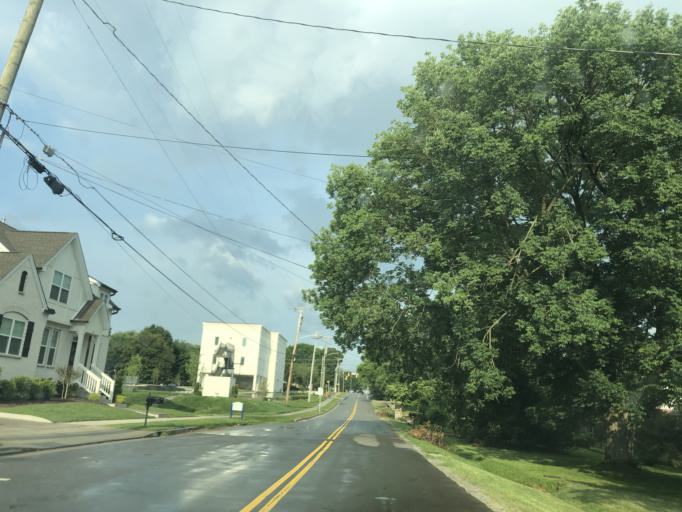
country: US
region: Tennessee
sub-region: Davidson County
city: Lakewood
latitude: 36.1552
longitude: -86.6676
